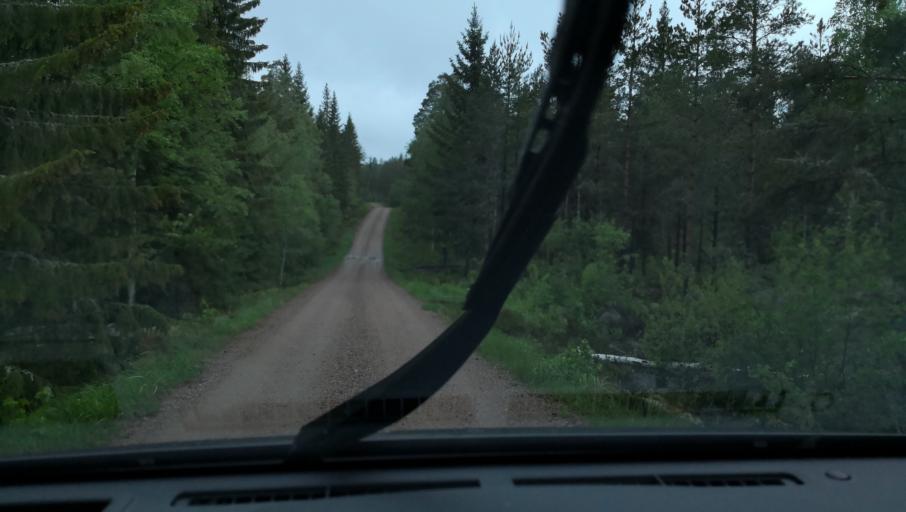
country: SE
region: Uppsala
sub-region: Enkopings Kommun
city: Orsundsbro
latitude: 59.9335
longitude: 17.3262
